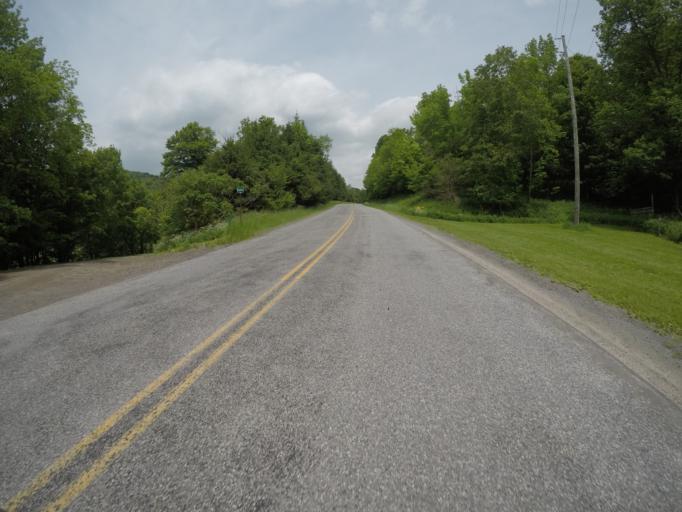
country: US
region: New York
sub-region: Delaware County
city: Stamford
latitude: 42.1765
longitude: -74.6734
